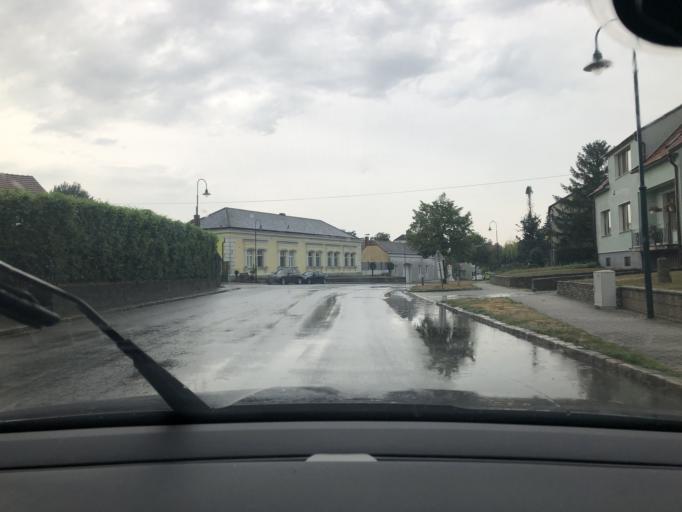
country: AT
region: Lower Austria
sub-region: Politischer Bezirk Ganserndorf
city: Angern an der March
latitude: 48.3061
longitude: 16.8315
